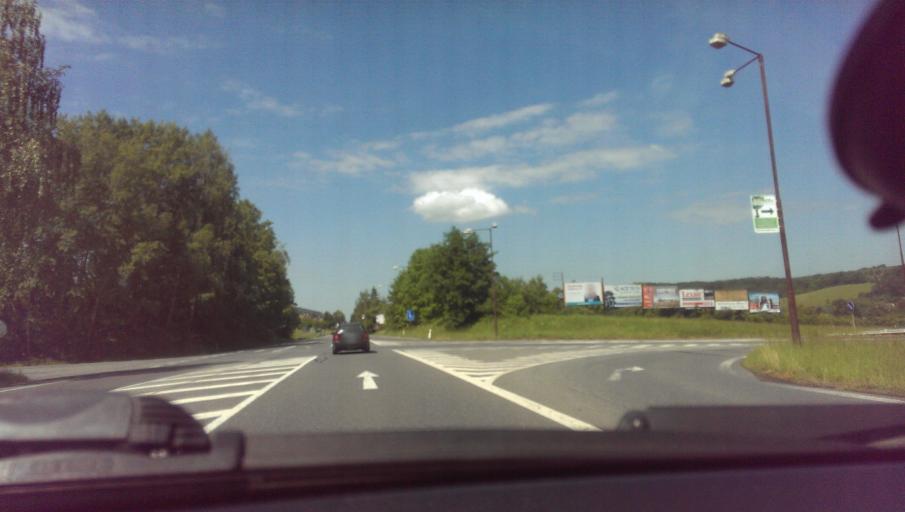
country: CZ
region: Zlin
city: Slusovice
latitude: 49.2126
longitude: 17.7788
